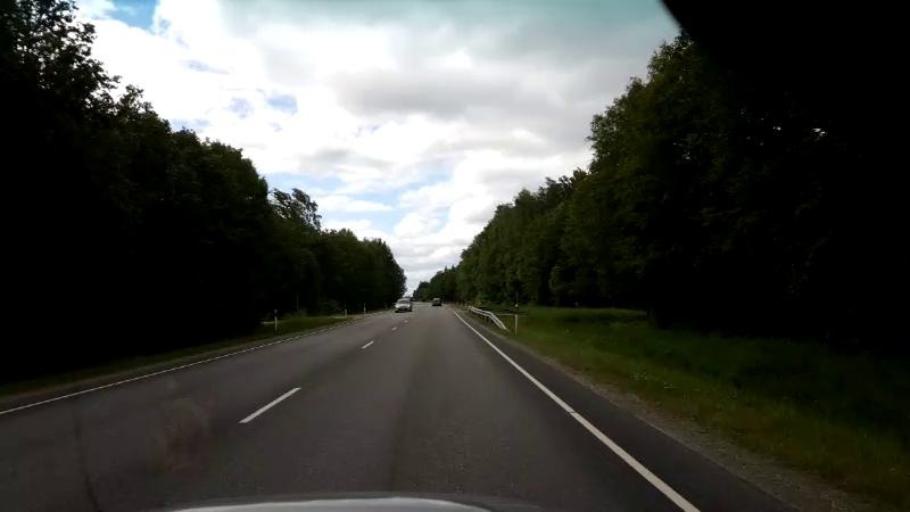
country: EE
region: Paernumaa
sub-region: Halinga vald
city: Parnu-Jaagupi
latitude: 58.6053
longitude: 24.5122
